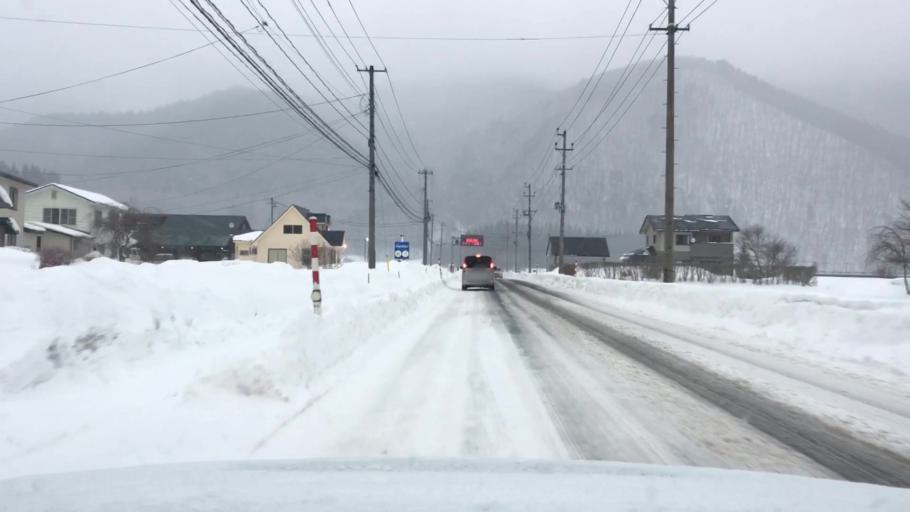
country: JP
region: Akita
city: Hanawa
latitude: 40.0776
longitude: 141.0219
